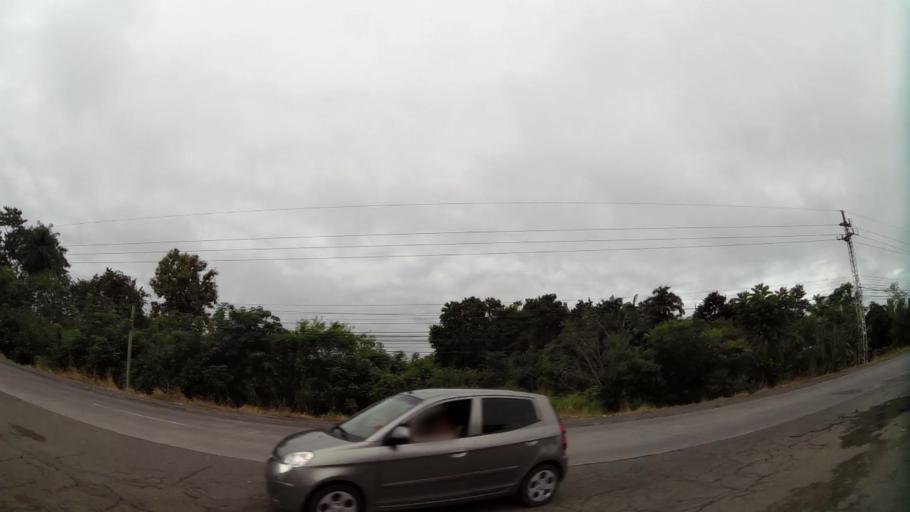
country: PA
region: Chiriqui
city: Boqueron
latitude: 8.4978
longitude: -82.5918
